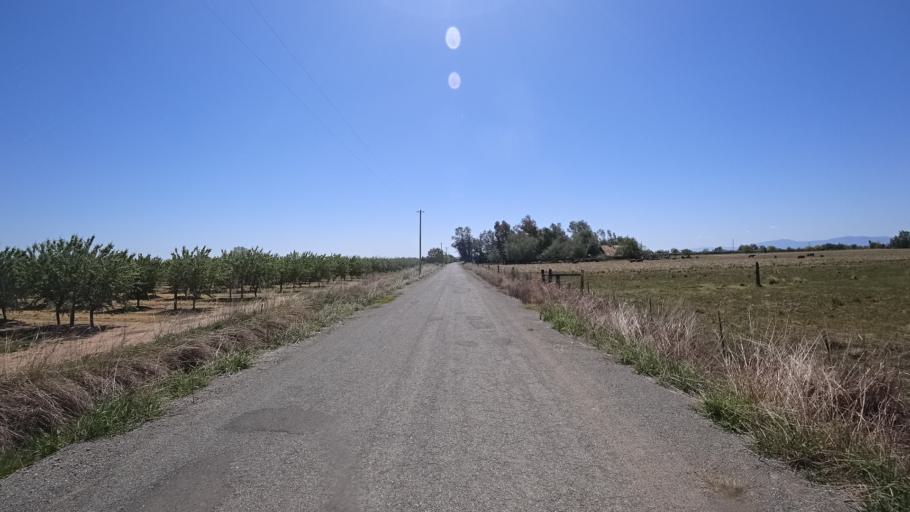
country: US
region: California
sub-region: Glenn County
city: Orland
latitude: 39.7931
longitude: -122.2159
